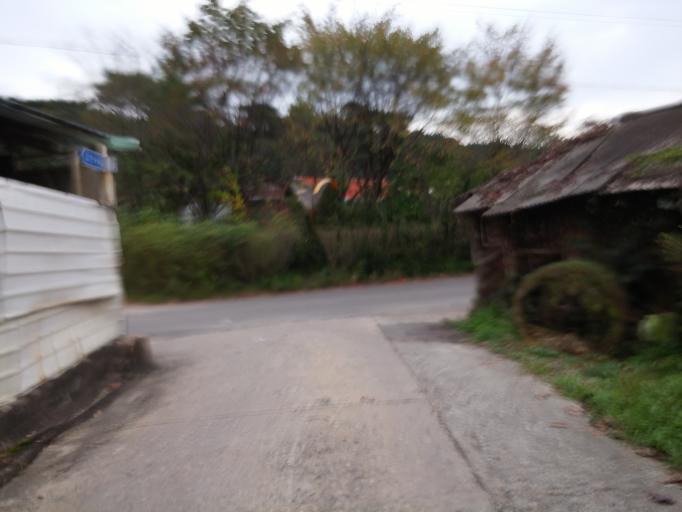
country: KR
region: Daejeon
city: Daejeon
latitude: 36.2661
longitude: 127.3320
